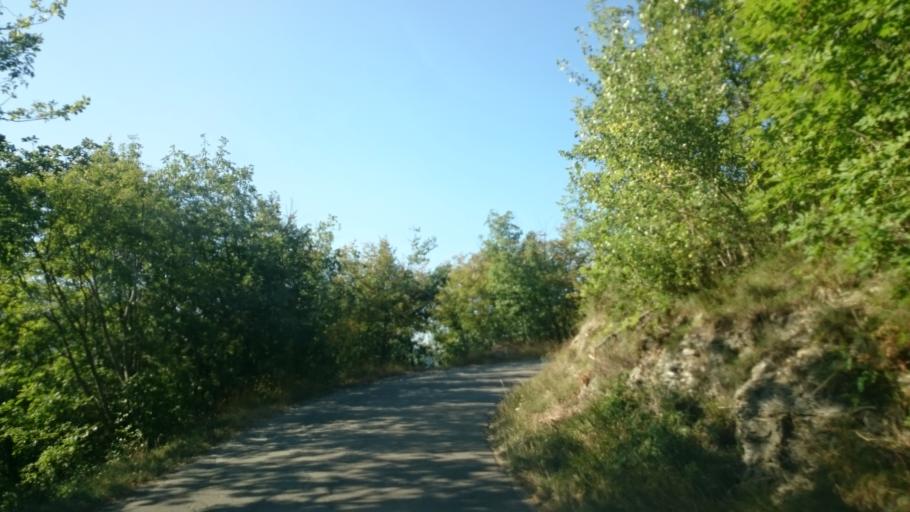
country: IT
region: Emilia-Romagna
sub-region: Provincia di Reggio Emilia
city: Villa Minozzo
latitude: 44.3211
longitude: 10.4682
